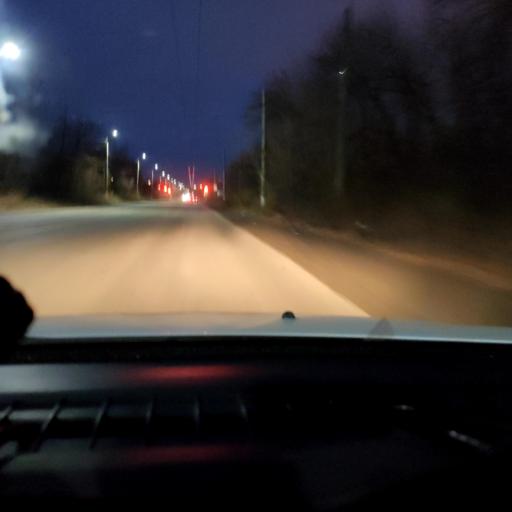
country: RU
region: Samara
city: Novokuybyshevsk
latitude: 53.0801
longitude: 49.9322
